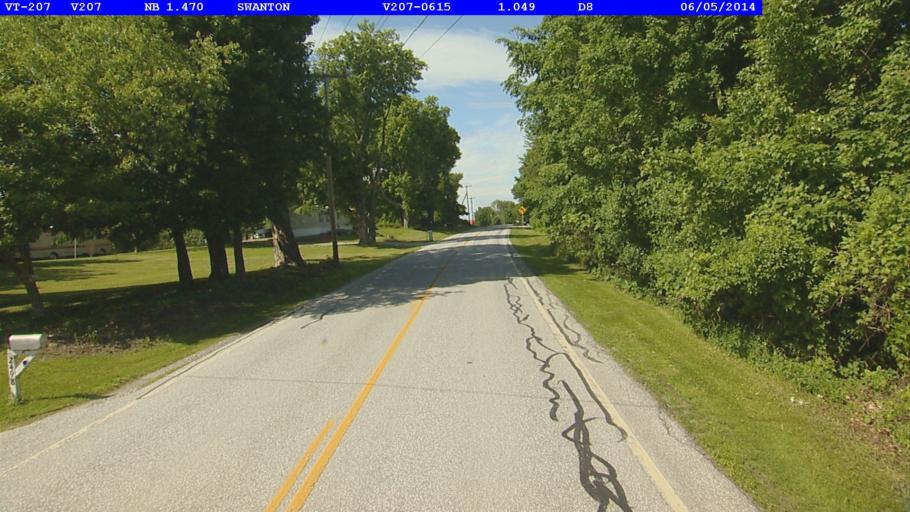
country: US
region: Vermont
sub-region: Franklin County
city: Saint Albans
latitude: 44.8602
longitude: -73.0749
